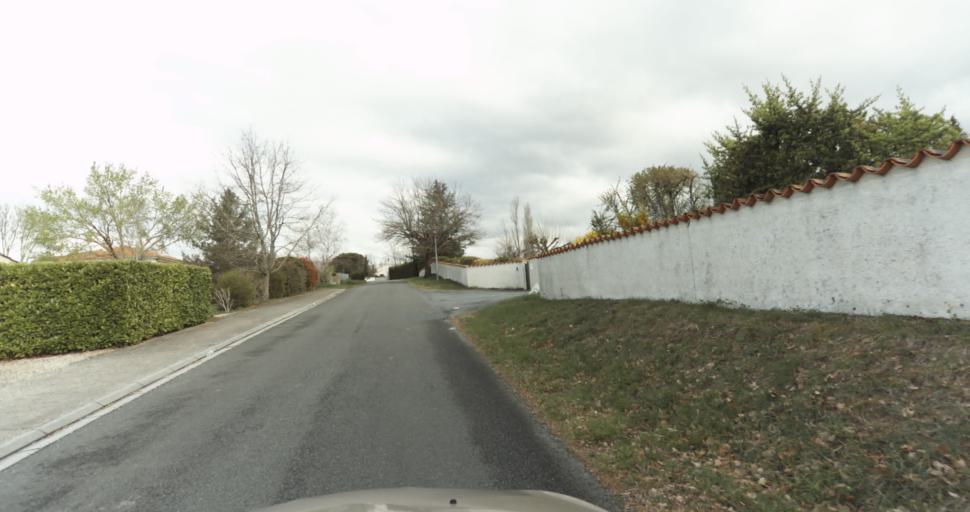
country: FR
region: Midi-Pyrenees
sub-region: Departement du Tarn
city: Puygouzon
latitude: 43.8996
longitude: 2.1769
